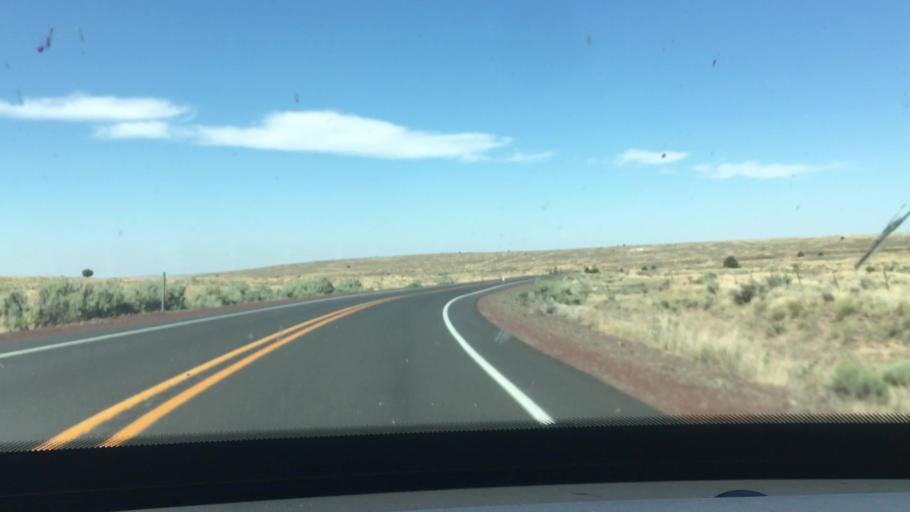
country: US
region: Oregon
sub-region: Sherman County
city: Moro
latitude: 45.0742
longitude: -120.6817
